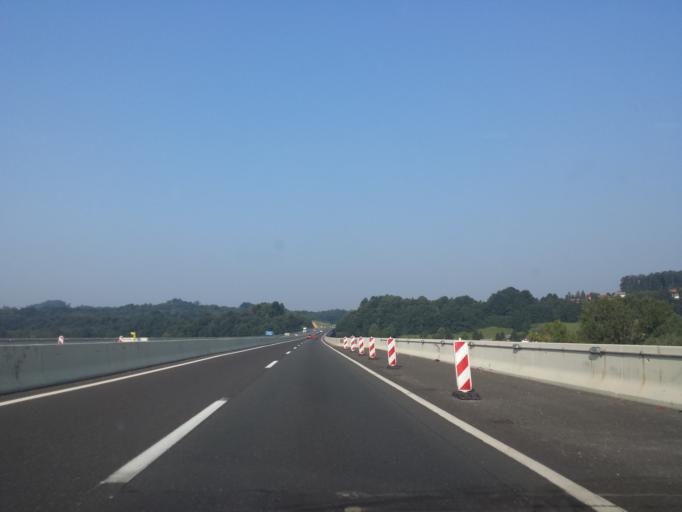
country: HR
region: Karlovacka
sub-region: Grad Karlovac
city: Karlovac
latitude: 45.5105
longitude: 15.5267
